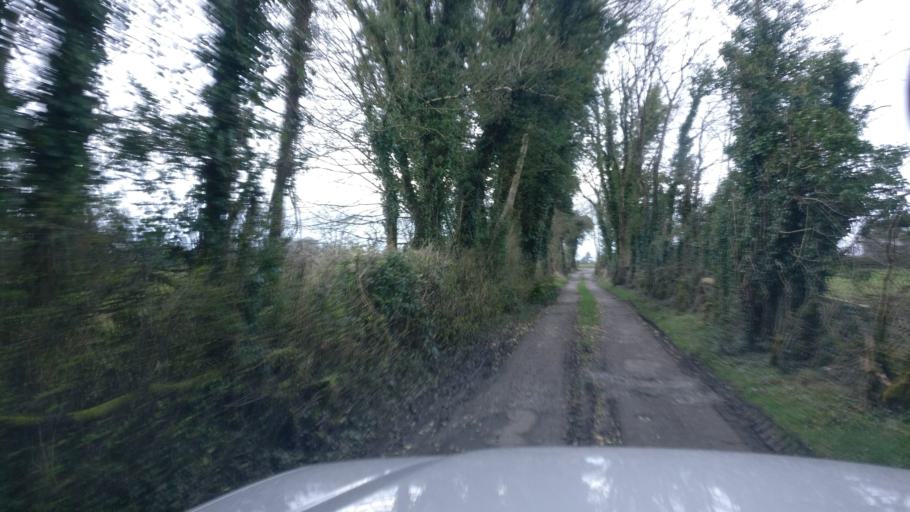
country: IE
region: Connaught
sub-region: County Galway
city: Loughrea
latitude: 53.2535
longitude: -8.4571
